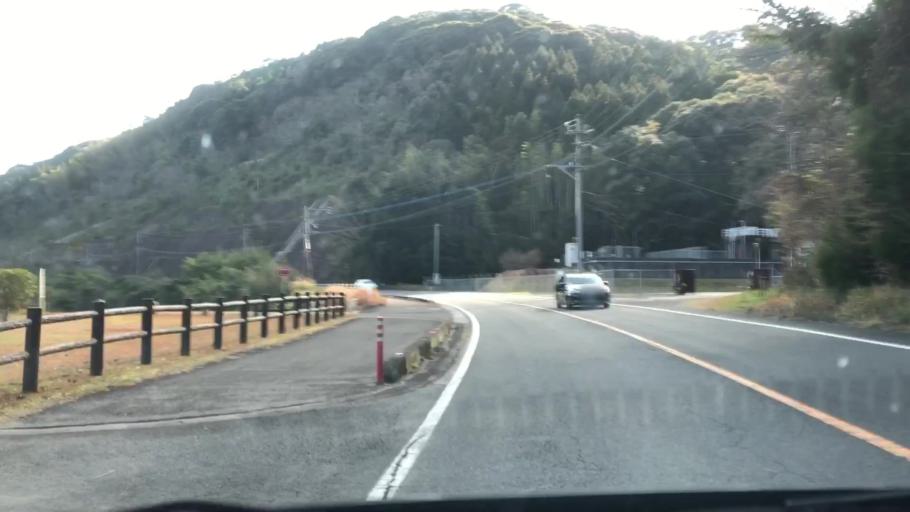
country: JP
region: Kagoshima
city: Satsumasendai
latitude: 31.8583
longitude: 130.3161
